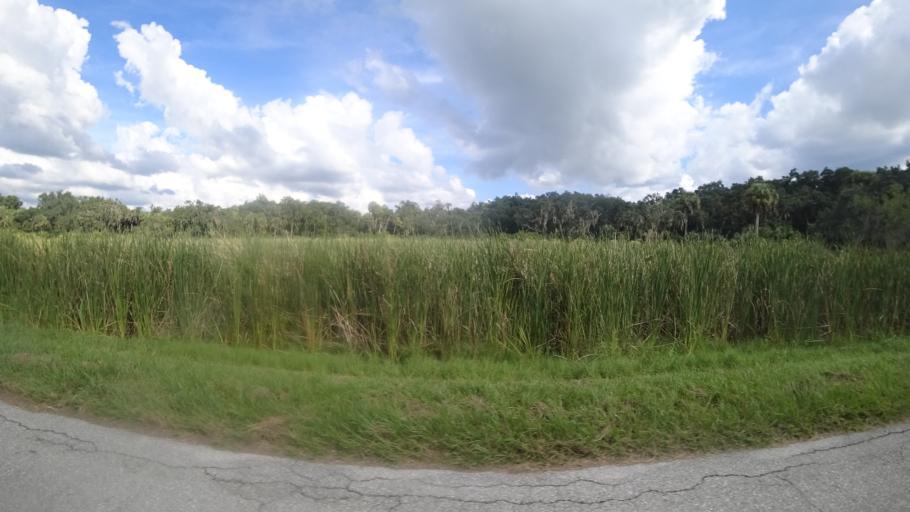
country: US
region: Florida
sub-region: Manatee County
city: Memphis
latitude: 27.5931
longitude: -82.5523
